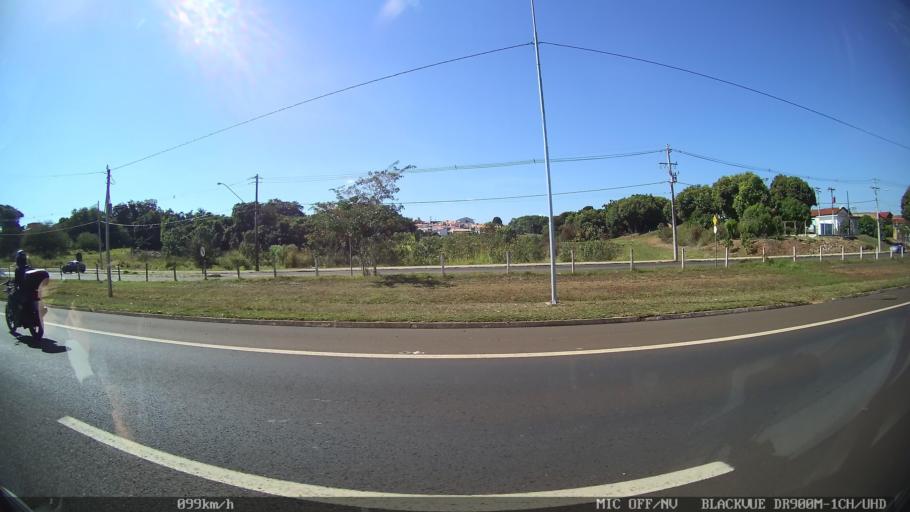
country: BR
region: Sao Paulo
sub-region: Franca
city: Franca
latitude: -20.4864
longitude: -47.4090
